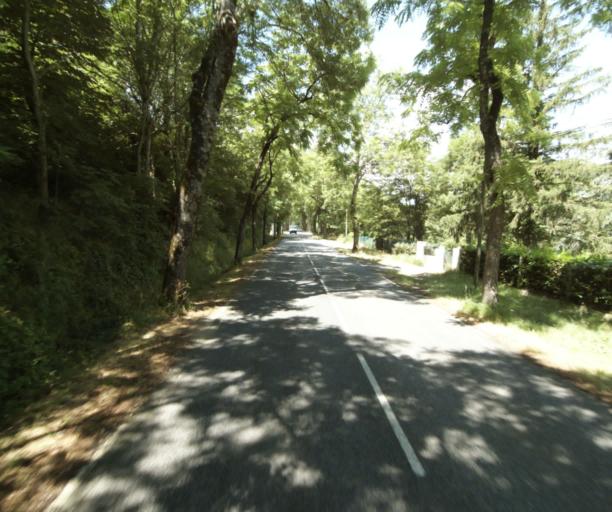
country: FR
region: Midi-Pyrenees
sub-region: Departement de la Haute-Garonne
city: Revel
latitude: 43.4470
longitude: 2.0110
